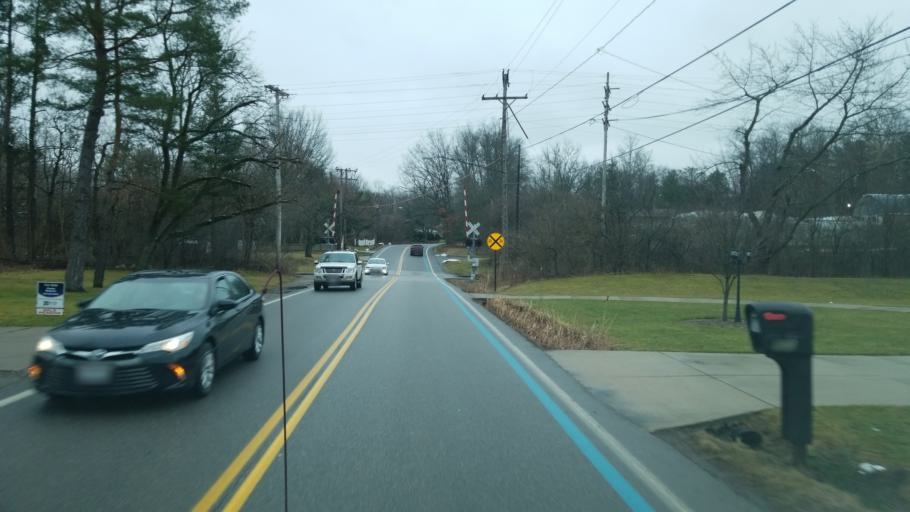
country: US
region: Ohio
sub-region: Summit County
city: Akron
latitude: 41.1234
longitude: -81.5488
